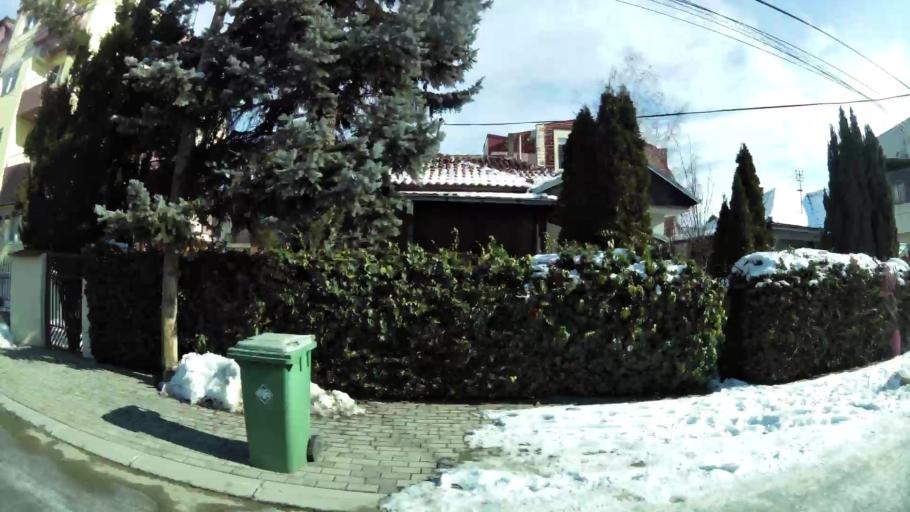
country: MK
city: Krushopek
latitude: 42.0019
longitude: 21.3696
